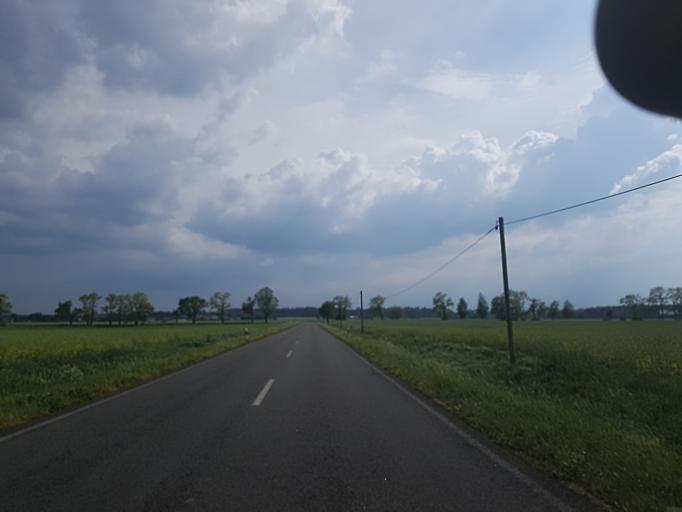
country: DE
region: Saxony-Anhalt
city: Rodleben
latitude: 51.9960
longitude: 12.2318
